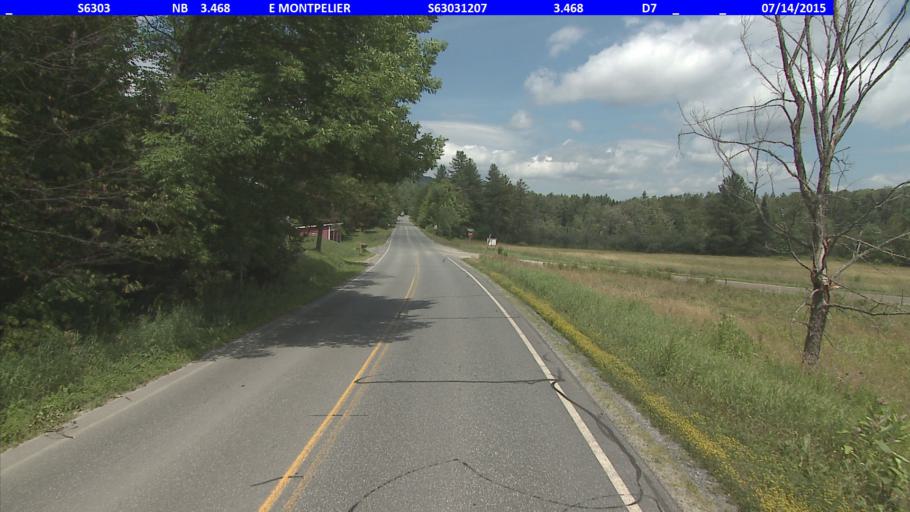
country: US
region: Vermont
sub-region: Washington County
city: Montpelier
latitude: 44.3172
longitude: -72.5274
